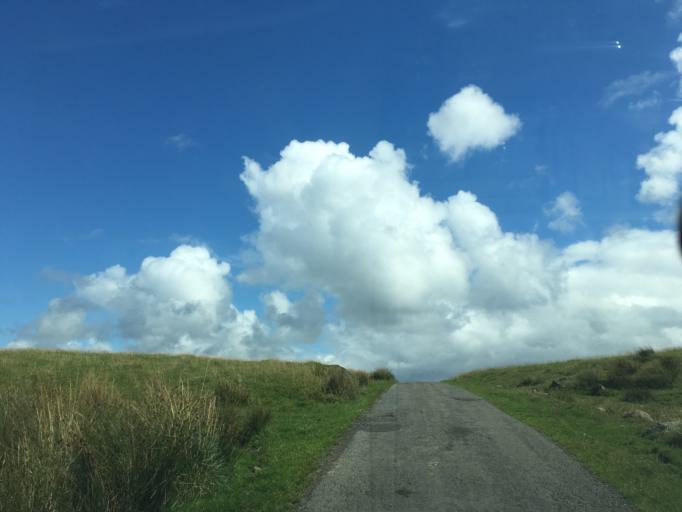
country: GB
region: Scotland
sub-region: Argyll and Bute
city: Isle Of Mull
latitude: 56.2206
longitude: -5.6485
